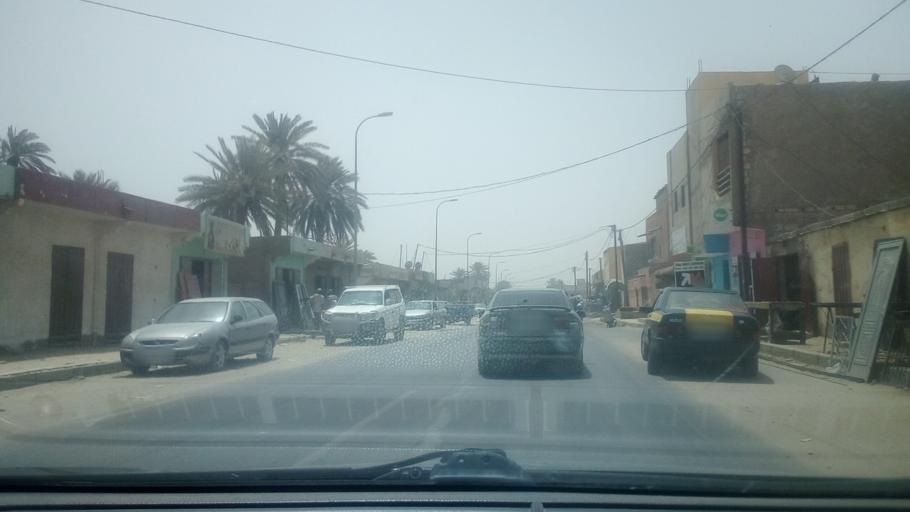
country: MR
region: Nouakchott
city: Nouakchott
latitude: 18.0821
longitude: -15.9893
